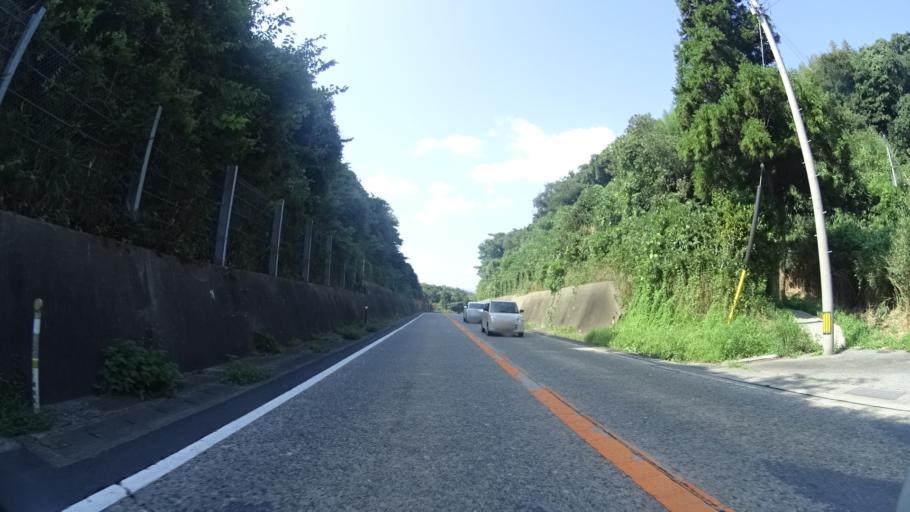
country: JP
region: Shimane
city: Gotsucho
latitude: 35.0585
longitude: 132.3166
